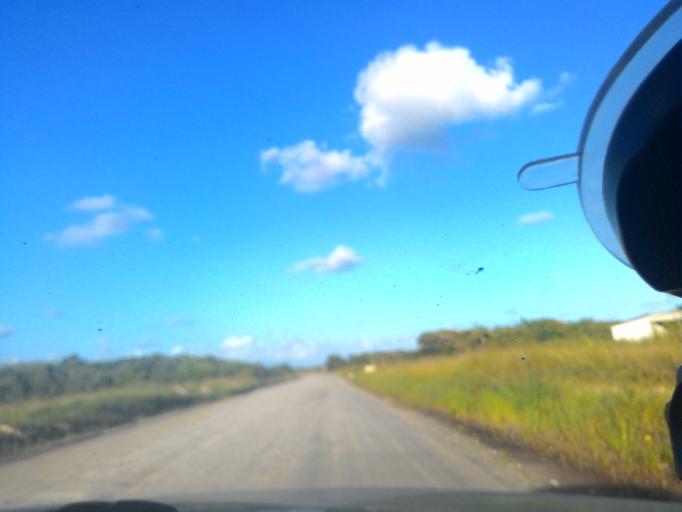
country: BR
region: Sao Paulo
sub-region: Pariquera-Acu
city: Pariquera Acu
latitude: -24.8806
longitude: -47.7370
